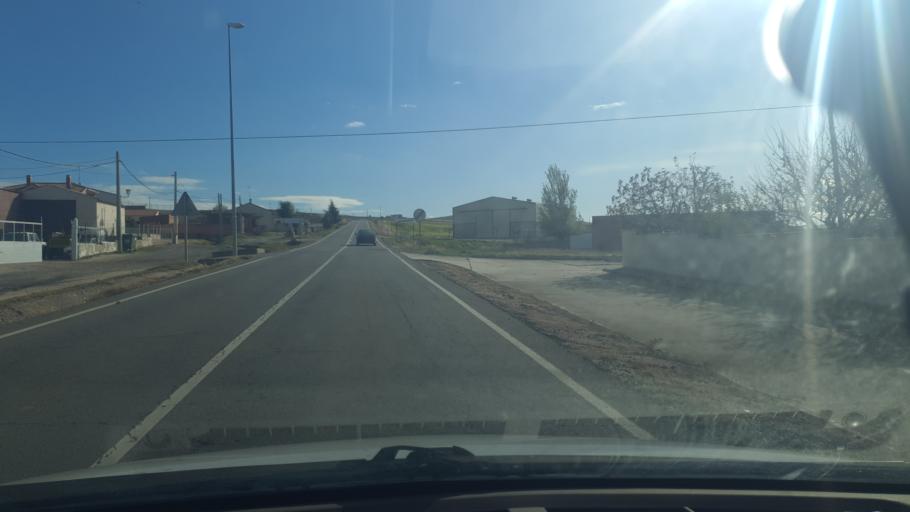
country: ES
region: Castille and Leon
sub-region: Provincia de Avila
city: Penalba de Avila
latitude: 40.7980
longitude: -4.7620
